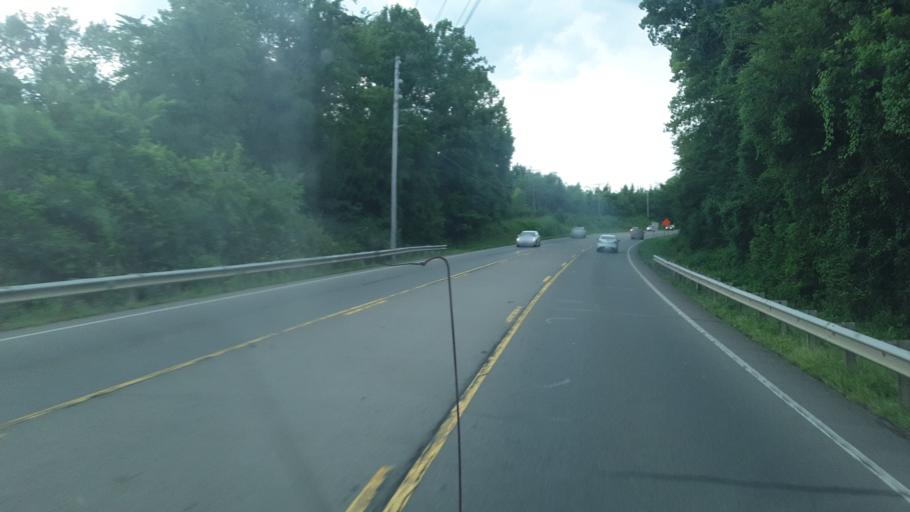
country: US
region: Tennessee
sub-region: Montgomery County
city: Clarksville
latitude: 36.5299
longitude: -87.2821
